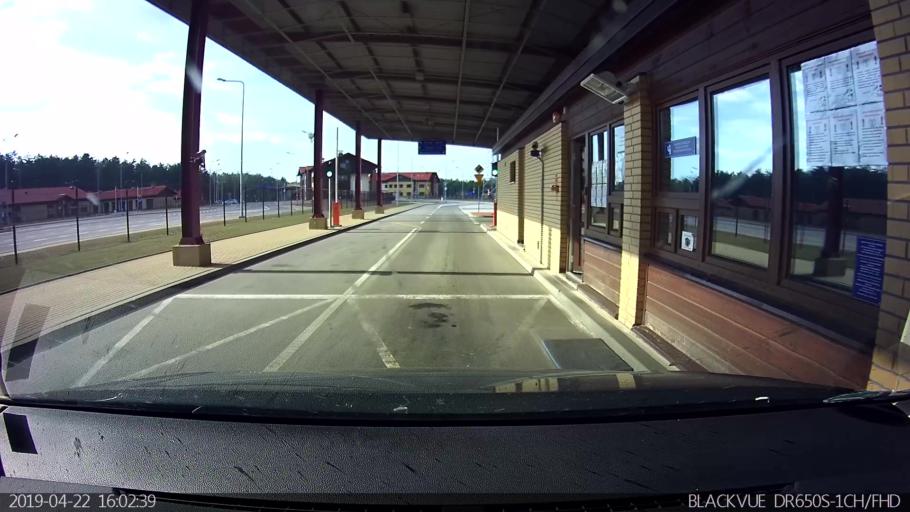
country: PL
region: Podlasie
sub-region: Powiat hajnowski
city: Czeremcha
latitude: 52.4751
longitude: 23.3571
